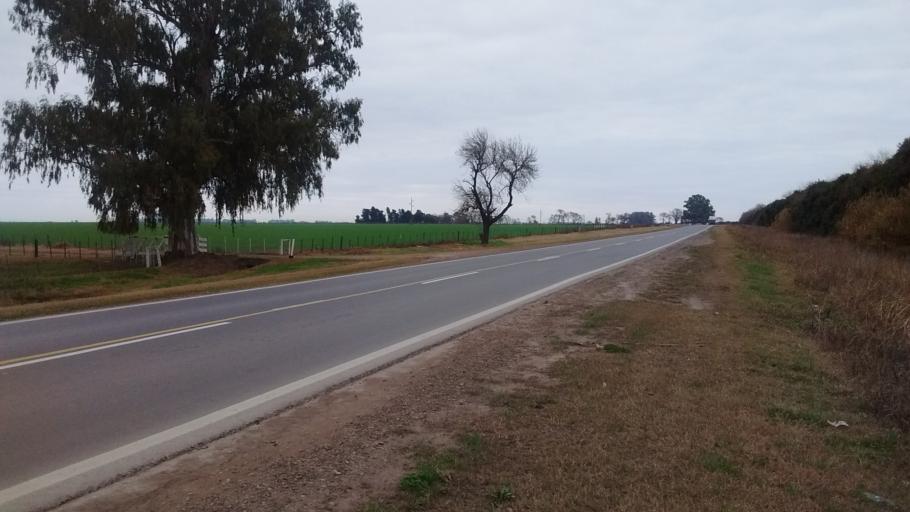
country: AR
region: Santa Fe
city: Las Rosas
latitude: -32.5323
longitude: -61.5508
